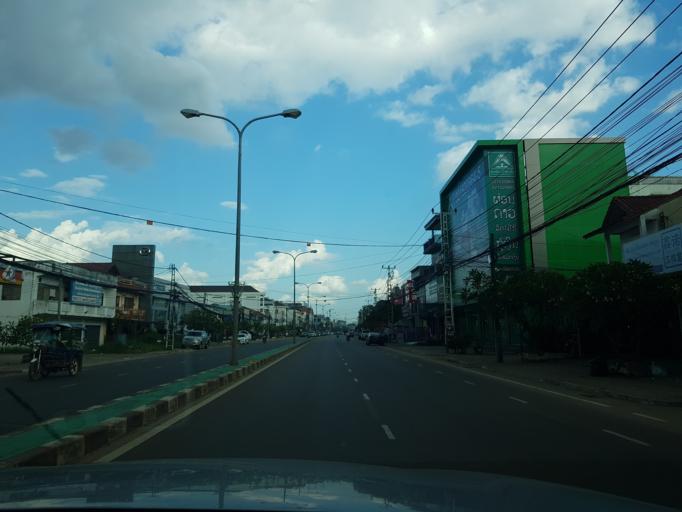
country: TH
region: Nong Khai
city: Si Chiang Mai
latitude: 17.9694
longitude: 102.5829
